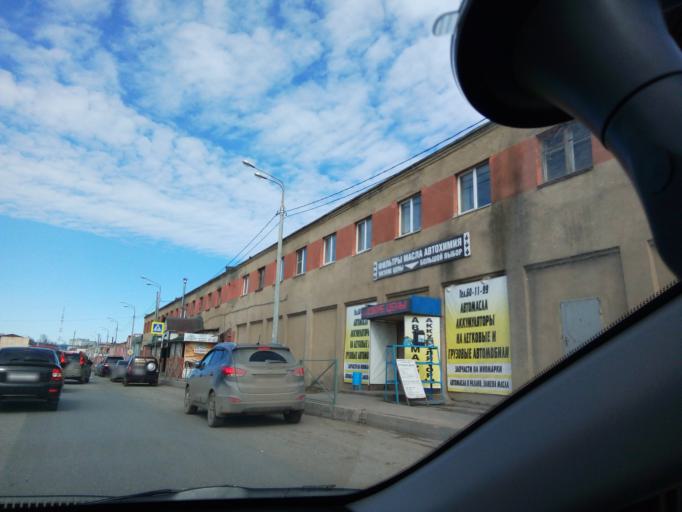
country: RU
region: Chuvashia
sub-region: Cheboksarskiy Rayon
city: Cheboksary
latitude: 56.1030
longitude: 47.2503
